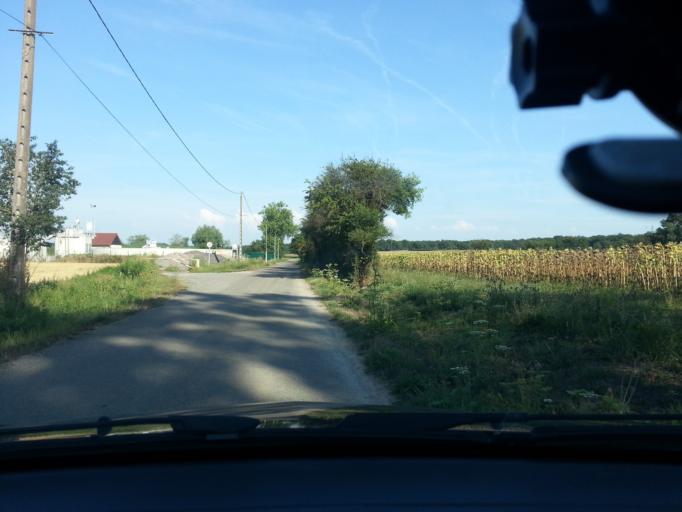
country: FR
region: Bourgogne
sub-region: Departement de Saone-et-Loire
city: Givry
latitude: 46.7783
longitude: 4.7587
